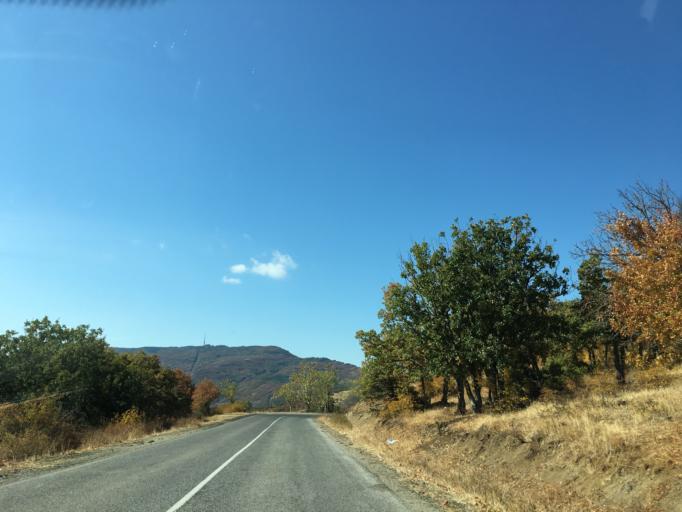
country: BG
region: Kurdzhali
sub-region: Obshtina Krumovgrad
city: Krumovgrad
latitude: 41.4703
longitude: 25.5325
